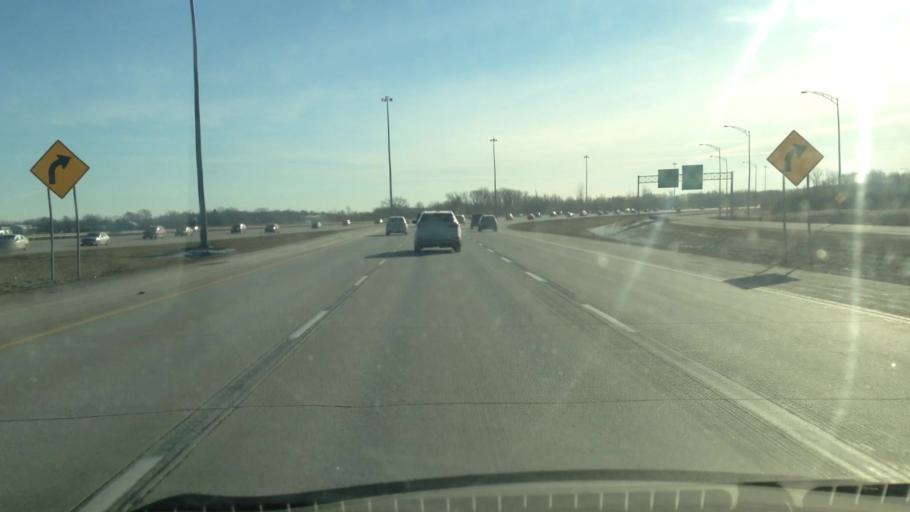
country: CA
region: Quebec
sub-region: Laurentides
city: Saint-Jerome
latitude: 45.7288
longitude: -73.9749
